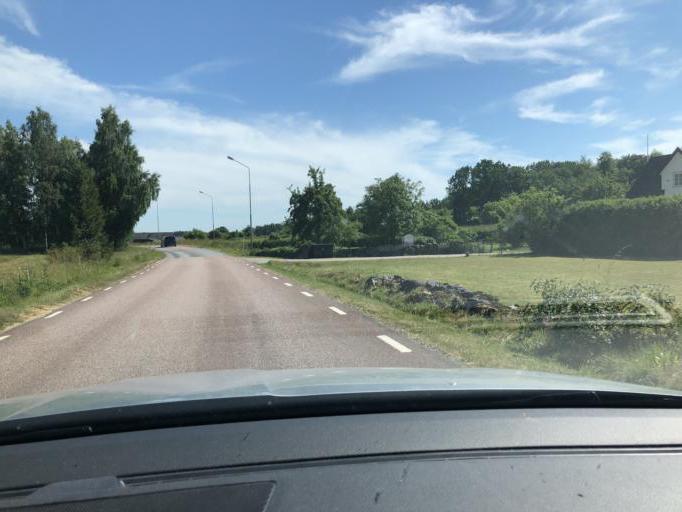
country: SE
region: Blekinge
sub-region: Solvesborgs Kommun
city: Soelvesborg
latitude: 56.1290
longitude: 14.6067
